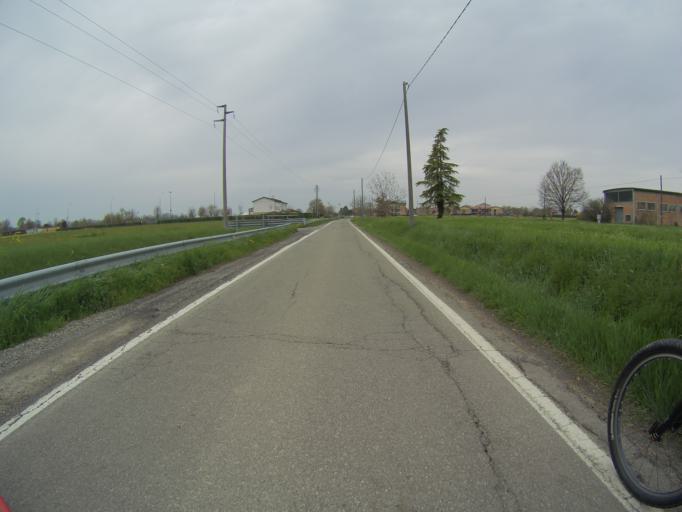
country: IT
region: Emilia-Romagna
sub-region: Provincia di Reggio Emilia
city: Bibbiano
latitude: 44.6566
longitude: 10.4801
